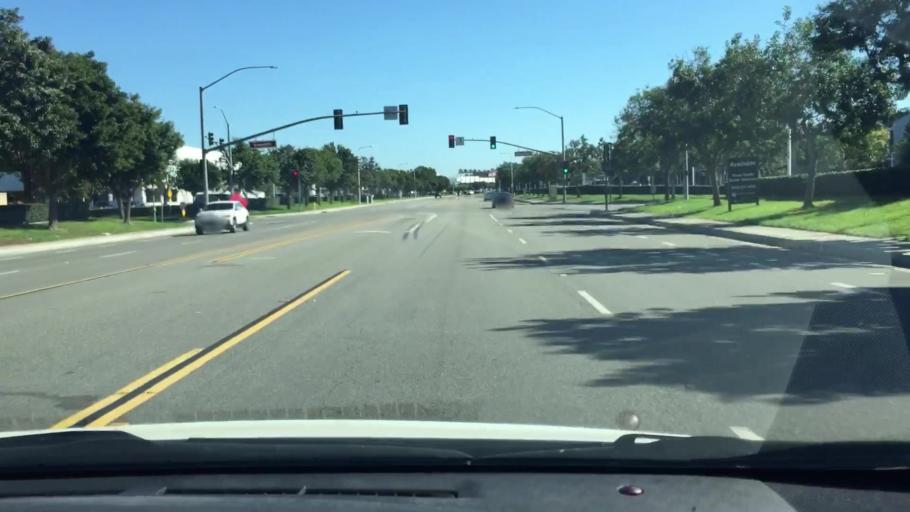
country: US
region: California
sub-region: Orange County
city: Laguna Woods
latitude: 33.6346
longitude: -117.7316
